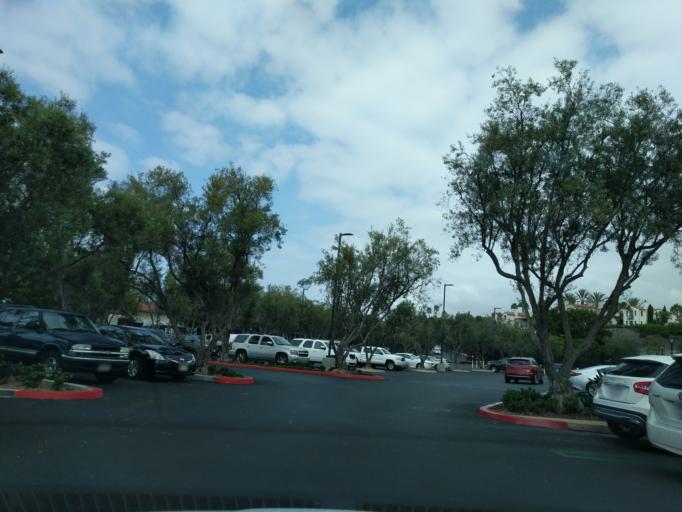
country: US
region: California
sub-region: Orange County
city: San Joaquin Hills
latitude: 33.5706
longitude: -117.8337
